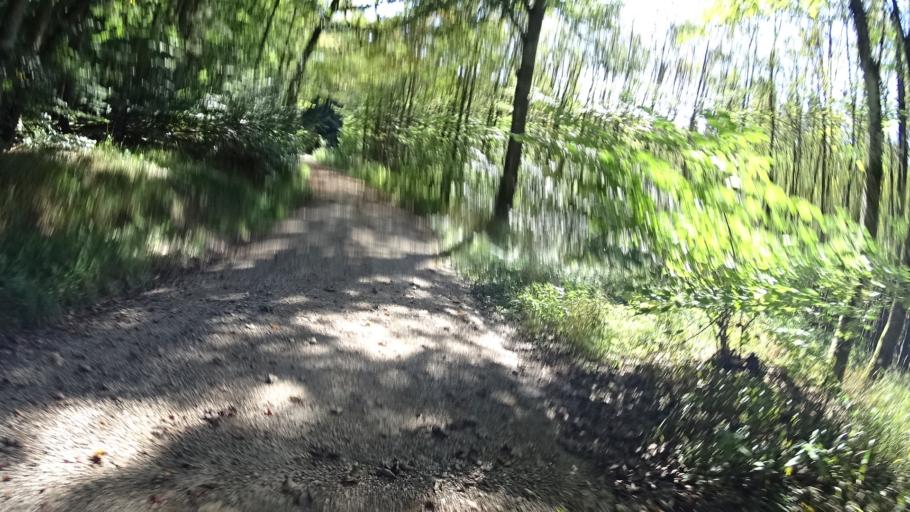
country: DE
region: Bavaria
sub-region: Upper Bavaria
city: Walting
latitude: 48.8857
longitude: 11.2988
